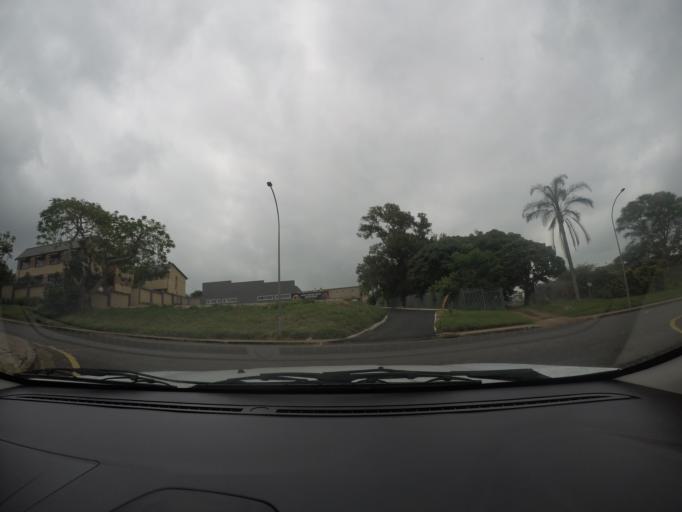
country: ZA
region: KwaZulu-Natal
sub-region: uThungulu District Municipality
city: Empangeni
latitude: -28.7426
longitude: 31.8942
